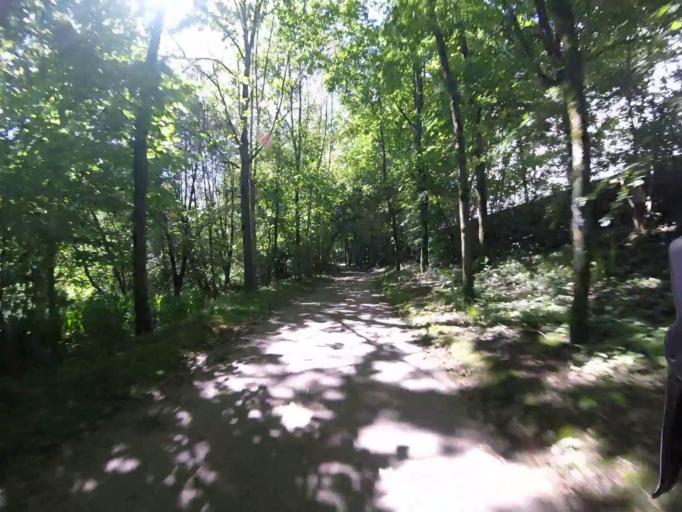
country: ES
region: Basque Country
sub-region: Provincia de Guipuzcoa
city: Irun
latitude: 43.3377
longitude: -1.7525
